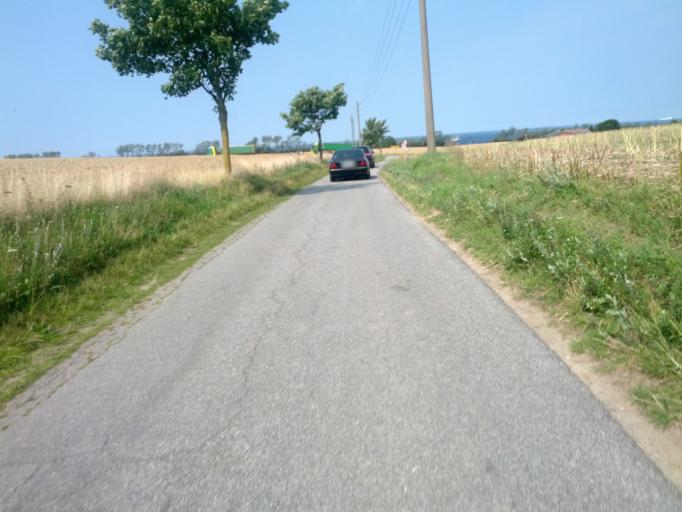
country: DE
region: Mecklenburg-Vorpommern
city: Bastorf
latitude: 54.1225
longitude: 11.6491
